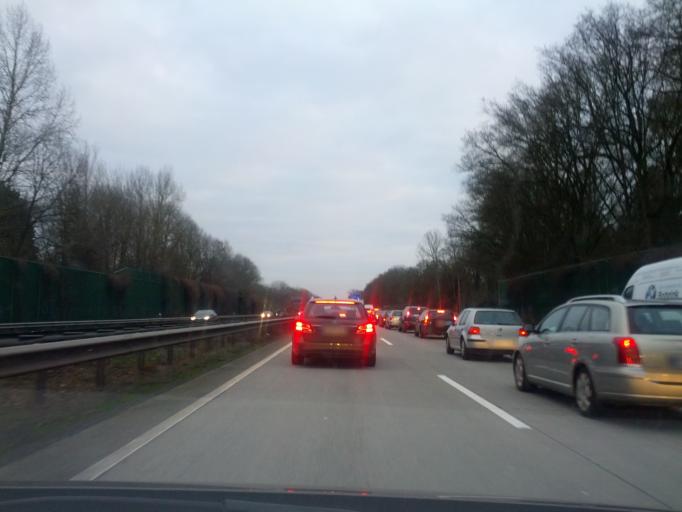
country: DE
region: Lower Saxony
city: Lilienthal
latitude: 53.0928
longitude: 8.8908
